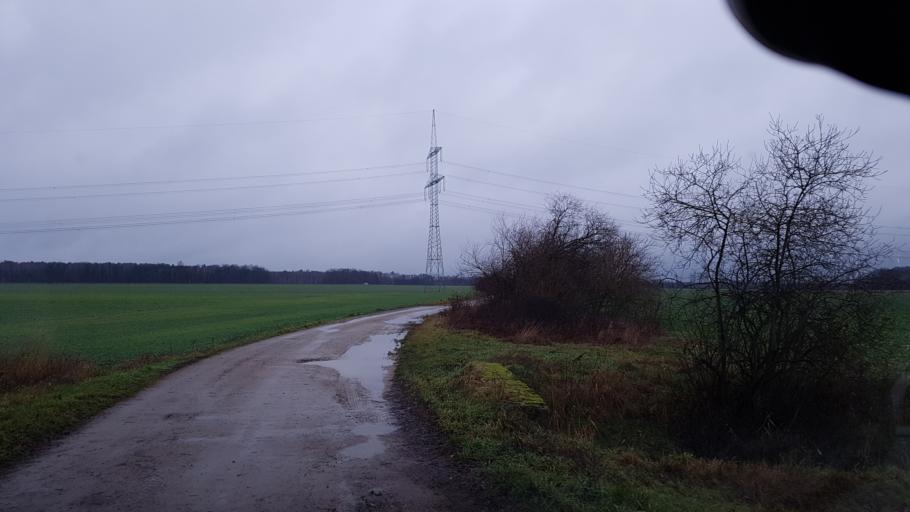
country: DE
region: Brandenburg
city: Sallgast
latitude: 51.6252
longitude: 13.8459
